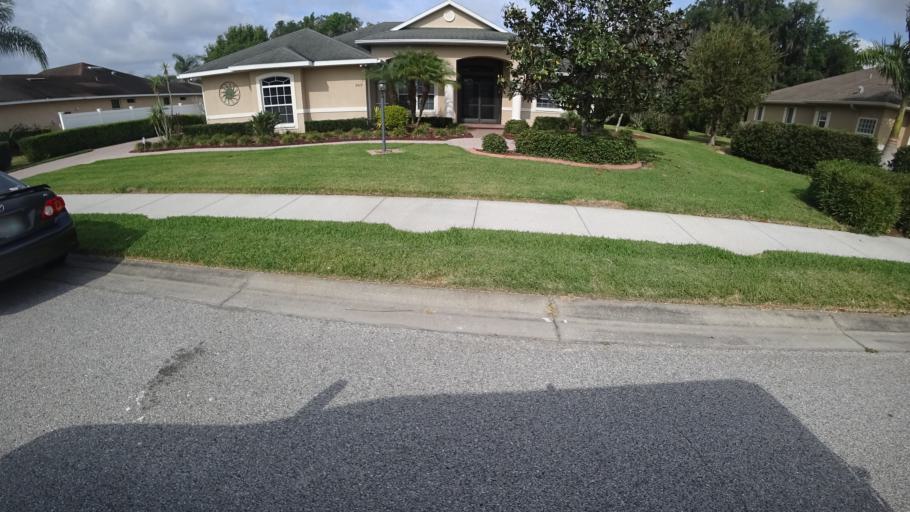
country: US
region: Florida
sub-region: Manatee County
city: Ellenton
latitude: 27.5635
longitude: -82.4734
